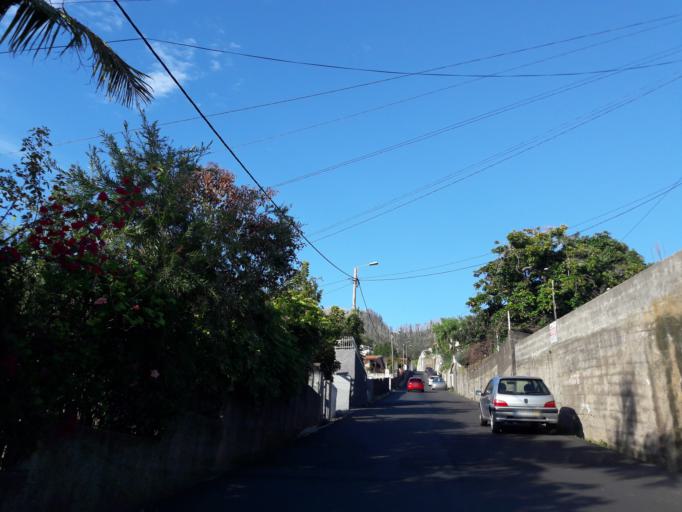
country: PT
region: Madeira
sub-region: Funchal
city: Nossa Senhora do Monte
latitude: 32.6725
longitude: -16.9210
